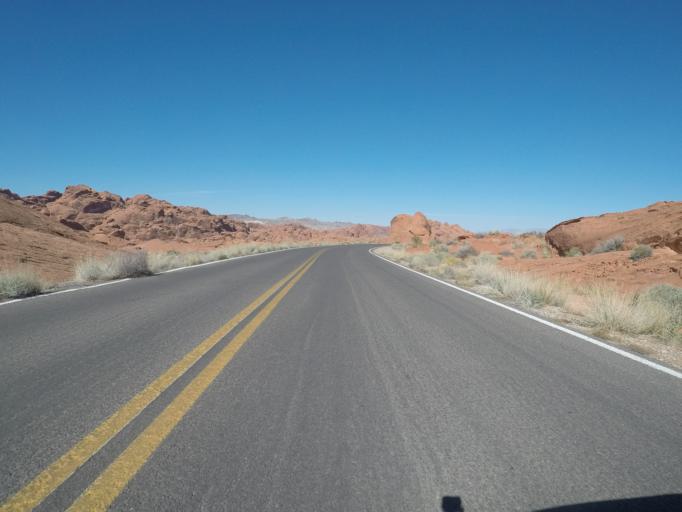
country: US
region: Nevada
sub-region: Clark County
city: Moapa Valley
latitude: 36.4896
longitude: -114.5334
